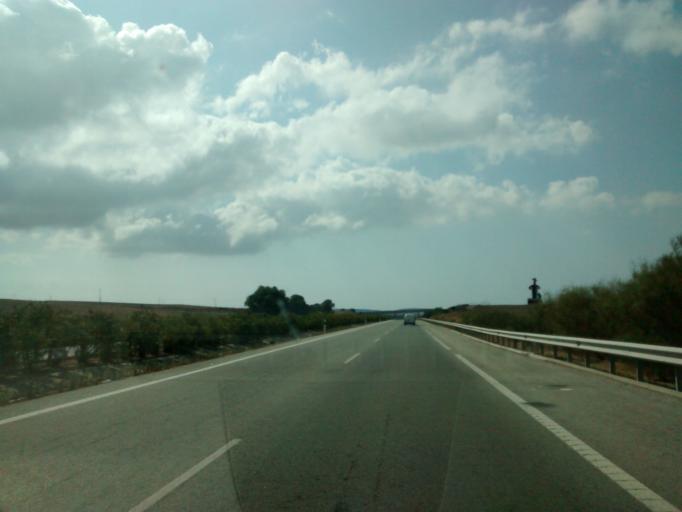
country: ES
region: Andalusia
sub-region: Provincia de Cadiz
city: Conil de la Frontera
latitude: 36.2600
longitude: -6.0293
